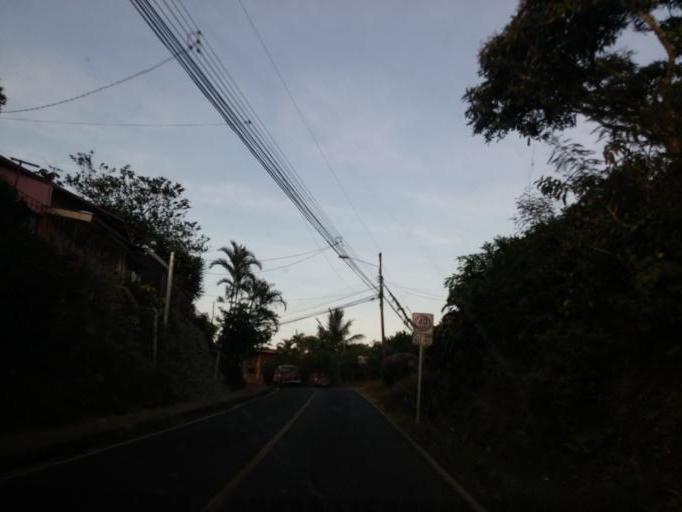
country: CR
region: Alajuela
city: Sabanilla
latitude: 10.0723
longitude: -84.2162
